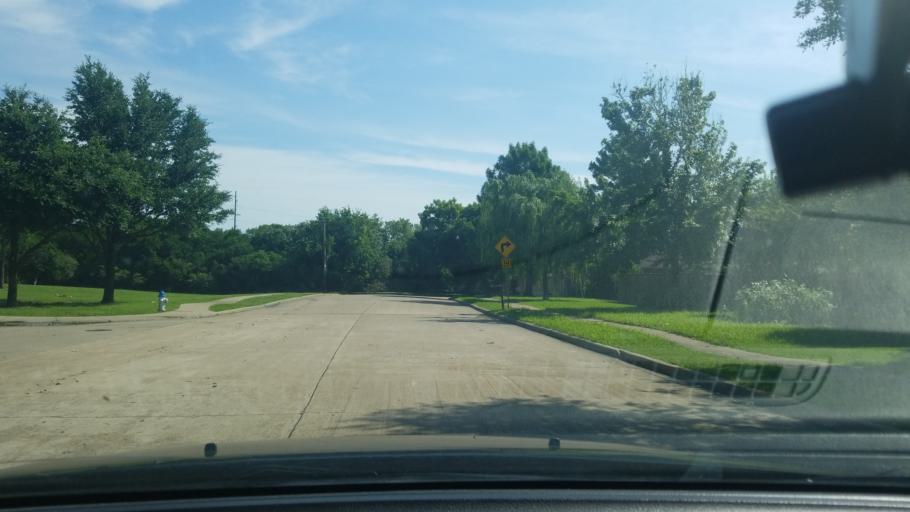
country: US
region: Texas
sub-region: Dallas County
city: Mesquite
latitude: 32.7734
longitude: -96.5797
